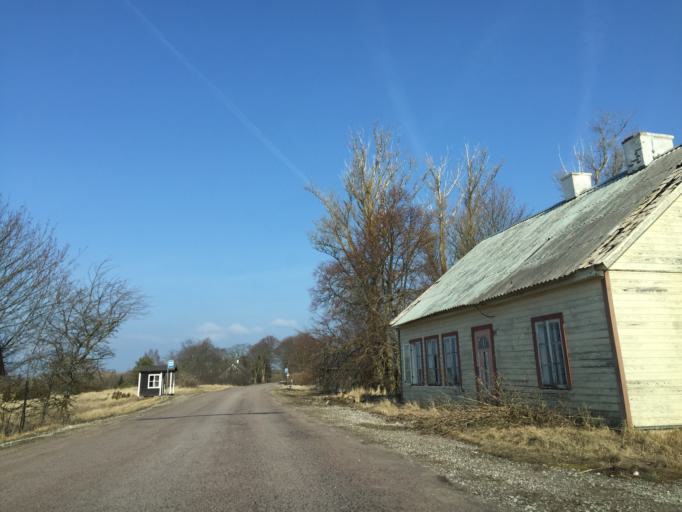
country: EE
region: Saare
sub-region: Kuressaare linn
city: Kuressaare
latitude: 58.0043
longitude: 22.0418
